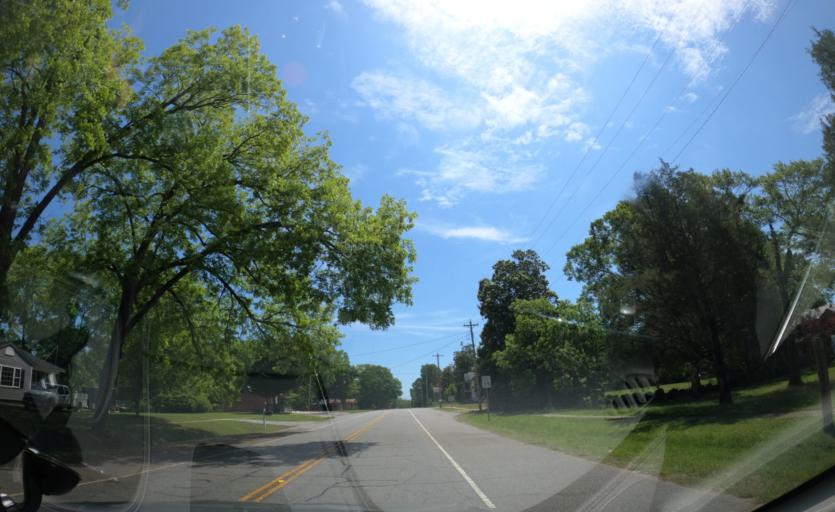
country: US
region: South Carolina
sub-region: Abbeville County
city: Lake Secession
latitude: 34.2103
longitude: -82.6459
